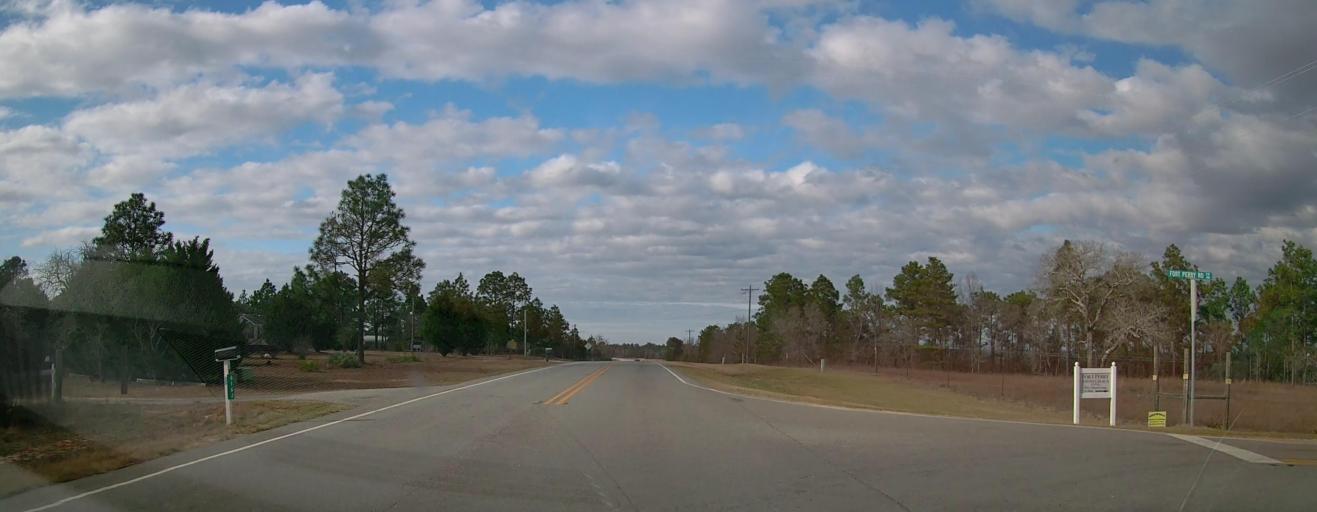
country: US
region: Georgia
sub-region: Marion County
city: Buena Vista
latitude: 32.4775
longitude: -84.5440
